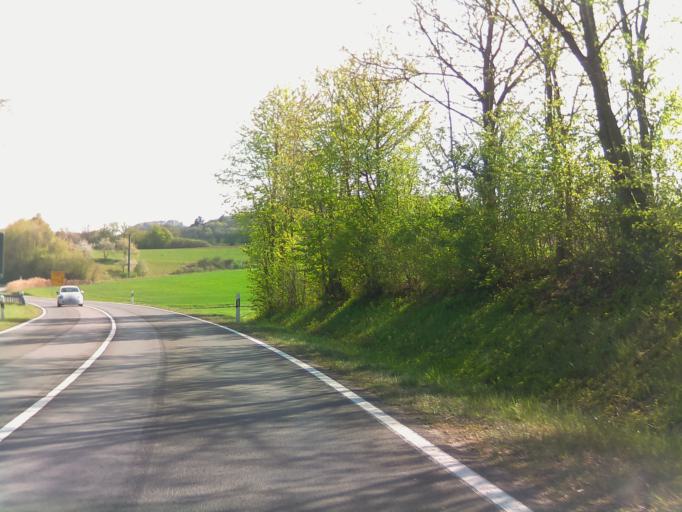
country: DE
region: Bavaria
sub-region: Regierungsbezirk Unterfranken
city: Zeil
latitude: 50.0538
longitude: 10.5880
